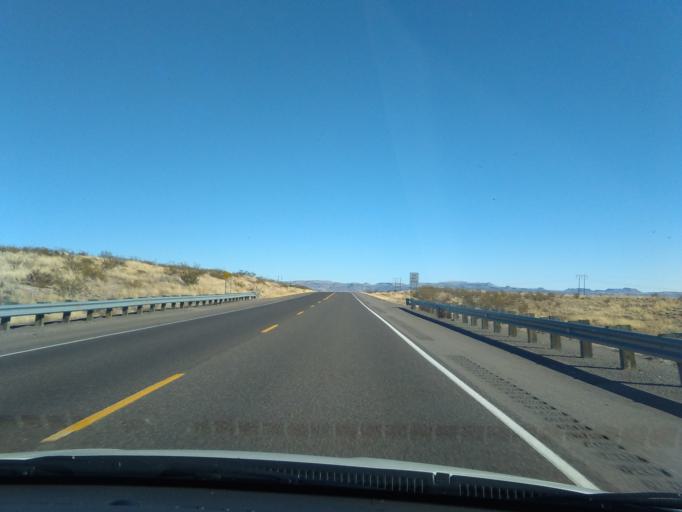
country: US
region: New Mexico
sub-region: Dona Ana County
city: Hatch
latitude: 32.5768
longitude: -107.4352
